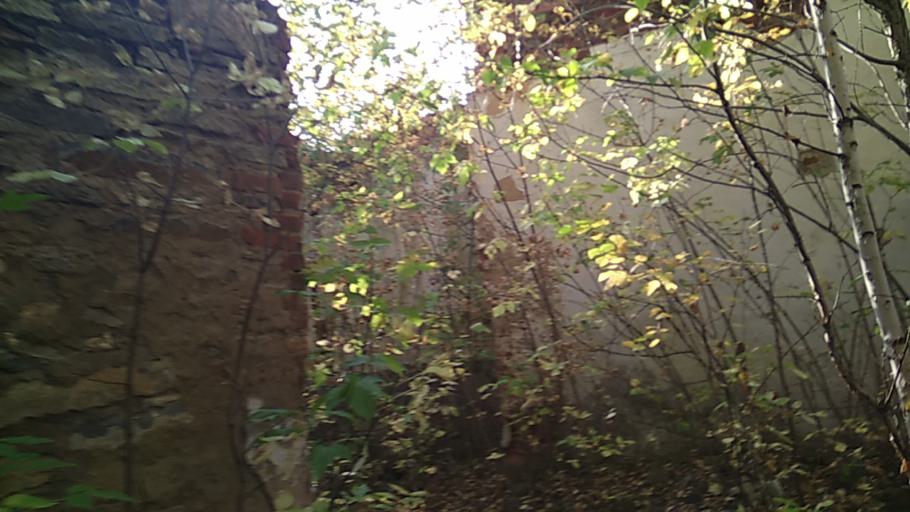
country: RU
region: Sverdlovsk
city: Pokrovskoye
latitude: 56.4332
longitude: 61.5975
